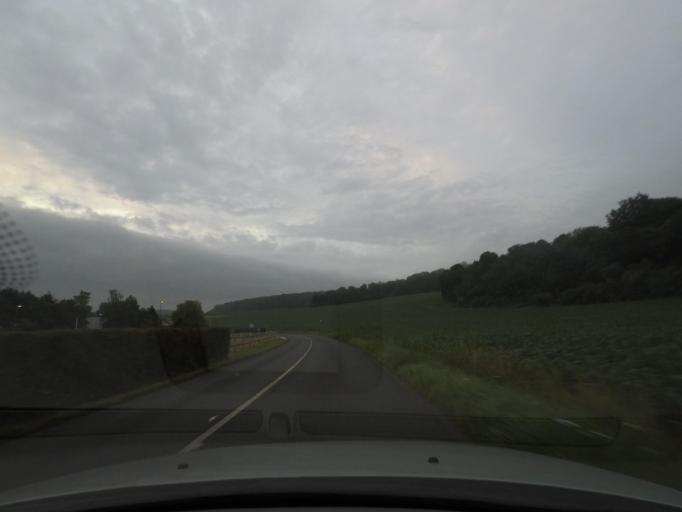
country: FR
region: Haute-Normandie
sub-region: Departement de la Seine-Maritime
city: Fontaine-le-Bourg
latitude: 49.5590
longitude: 1.1430
